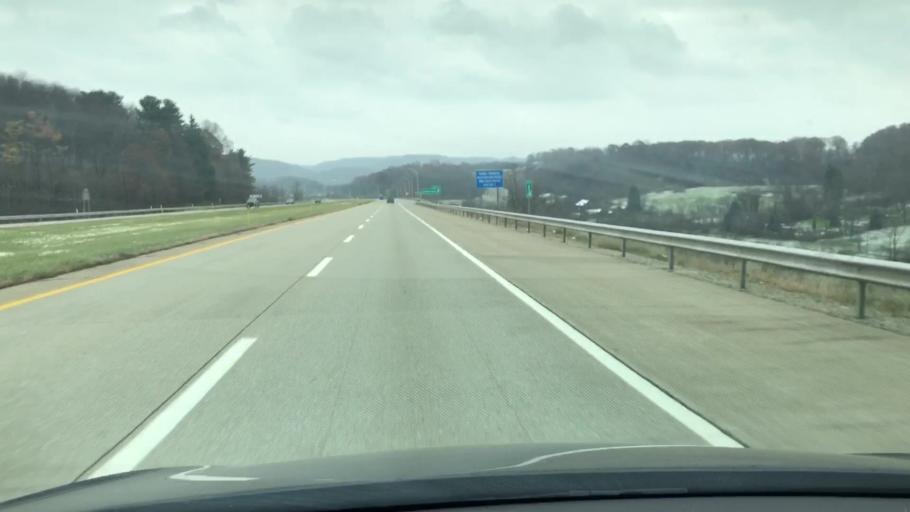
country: US
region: Pennsylvania
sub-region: Westmoreland County
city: New Stanton
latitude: 40.2430
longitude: -79.6073
